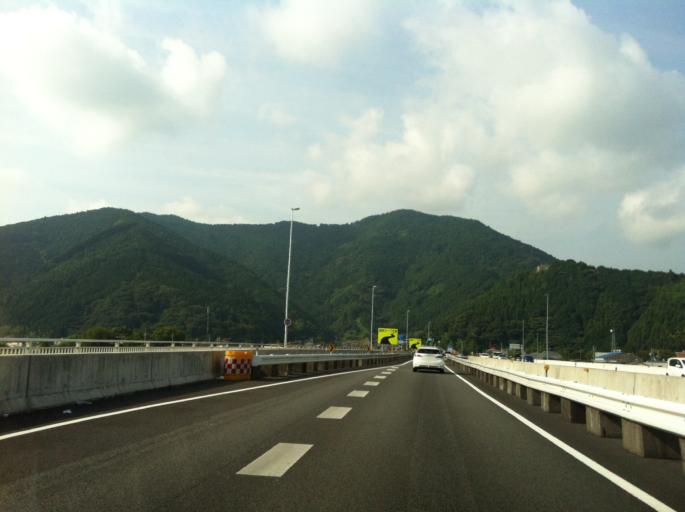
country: JP
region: Shizuoka
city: Shizuoka-shi
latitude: 34.9756
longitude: 138.3472
